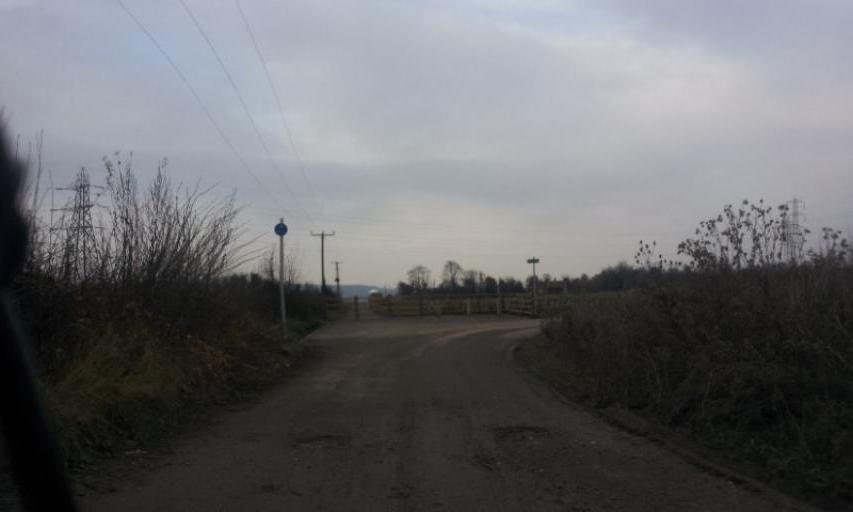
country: GB
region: England
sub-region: Kent
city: Snodland
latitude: 51.3325
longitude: 0.4621
